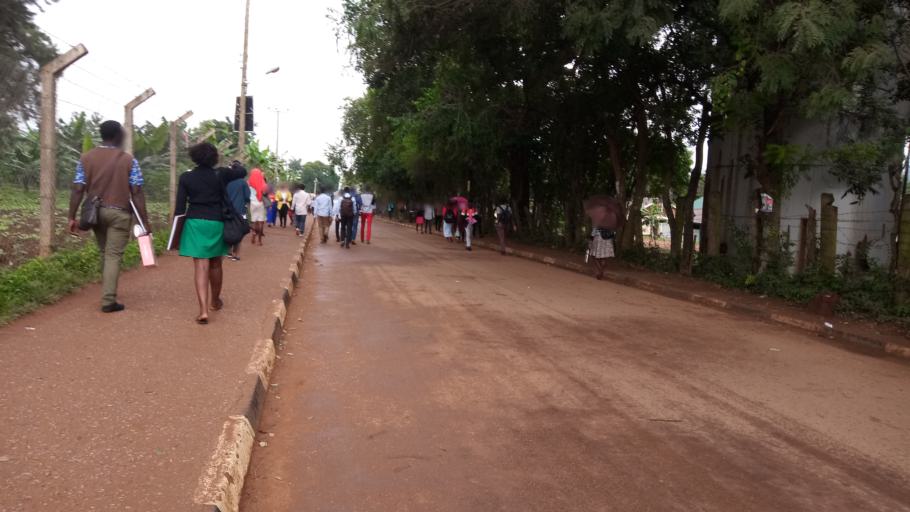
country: UG
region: Central Region
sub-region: Wakiso District
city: Kireka
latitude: 0.3455
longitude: 32.6334
